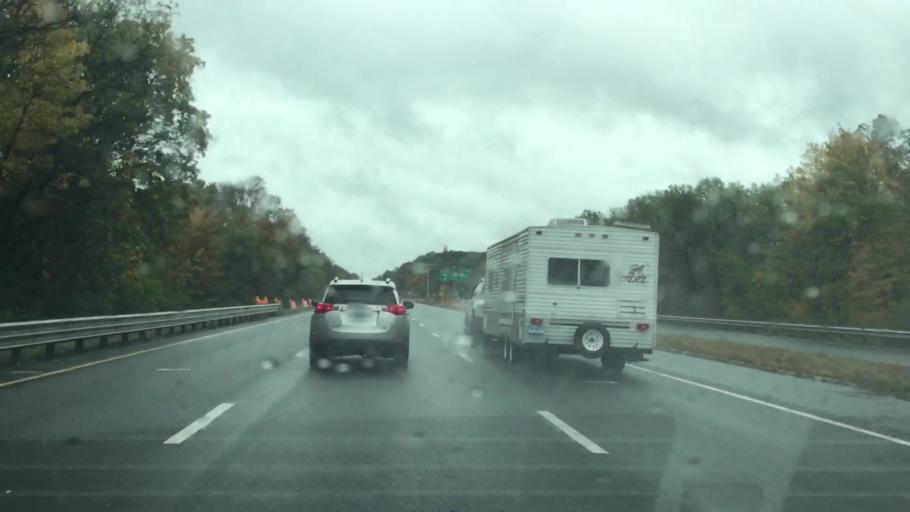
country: US
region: Massachusetts
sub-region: Essex County
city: Haverhill
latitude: 42.7813
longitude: -71.1167
